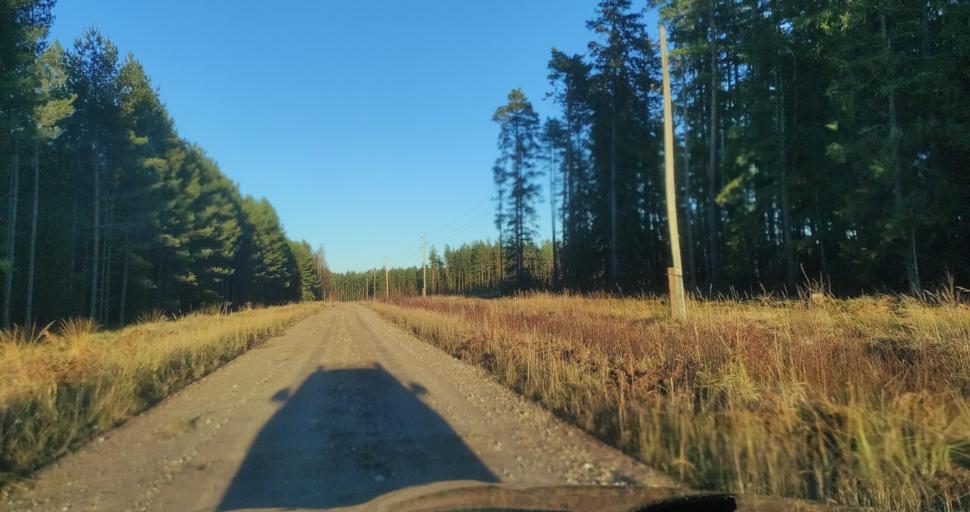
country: LV
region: Dundaga
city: Dundaga
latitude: 57.3696
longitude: 22.0718
